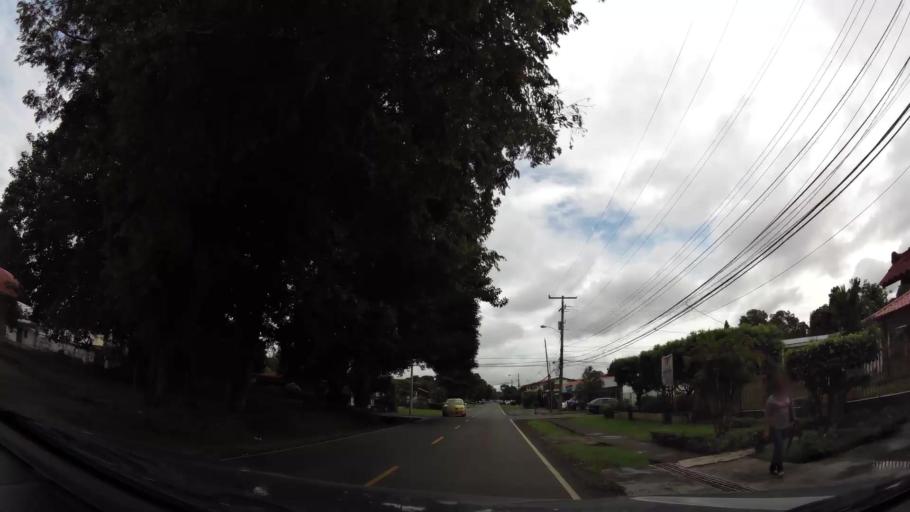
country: PA
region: Chiriqui
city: David
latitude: 8.4261
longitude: -82.4410
